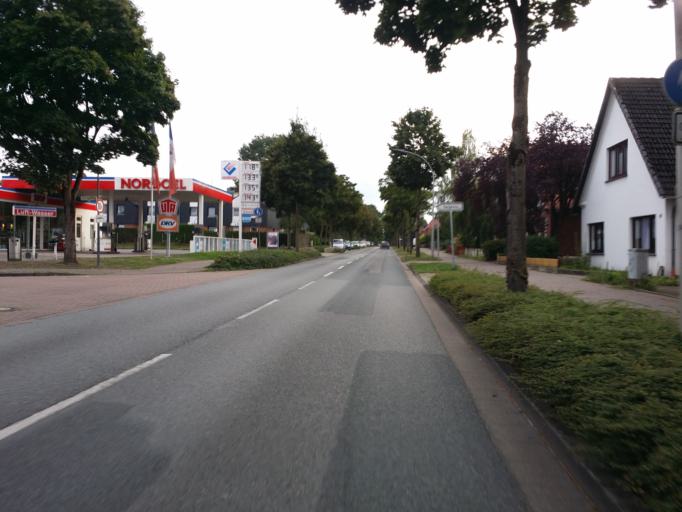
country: DE
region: Lower Saxony
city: Bremervorde
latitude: 53.4785
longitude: 9.1390
